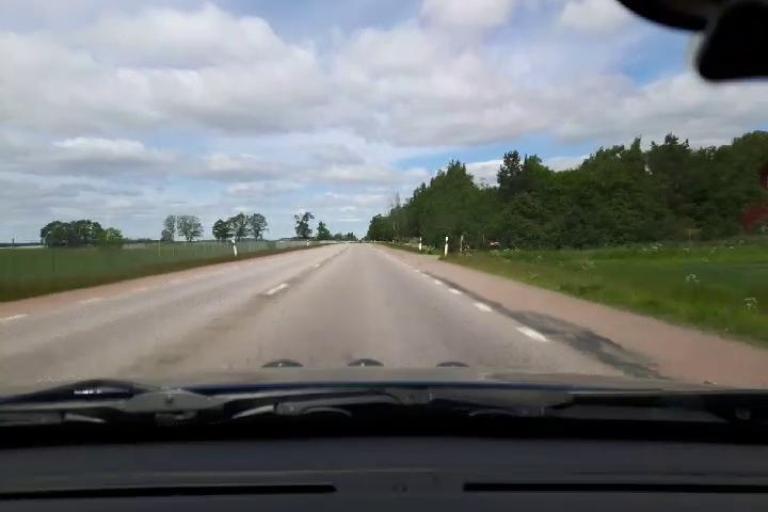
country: SE
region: Uppsala
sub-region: Uppsala Kommun
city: Gamla Uppsala
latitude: 59.8902
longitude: 17.6173
